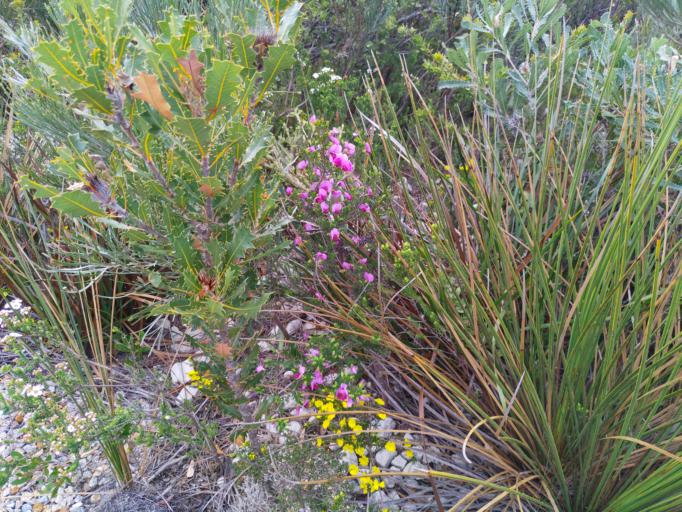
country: AU
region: Western Australia
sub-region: Ravensthorpe
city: Ravensthorpe
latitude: -33.9240
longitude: 120.0303
